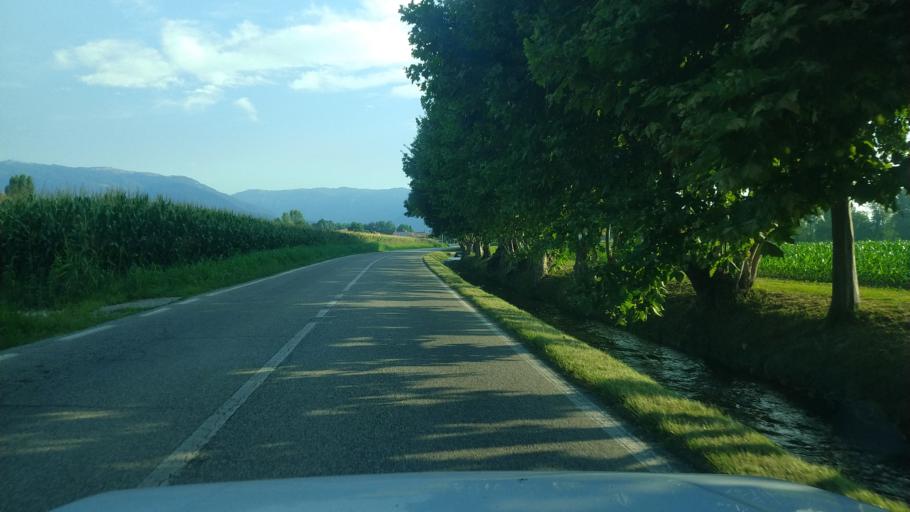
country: IT
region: Veneto
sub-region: Provincia di Vicenza
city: Cartigliano
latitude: 45.7248
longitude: 11.7226
